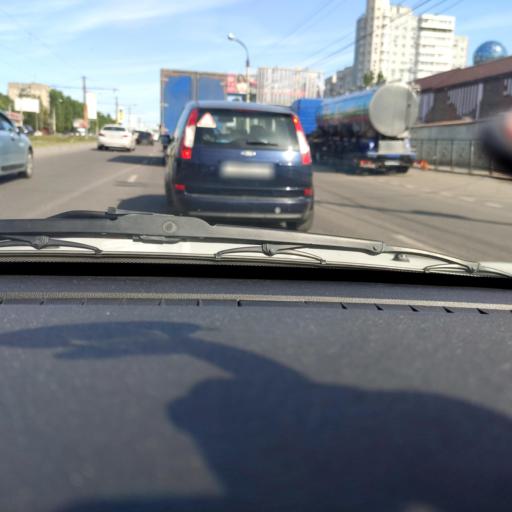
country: RU
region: Voronezj
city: Voronezh
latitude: 51.6868
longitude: 39.2542
